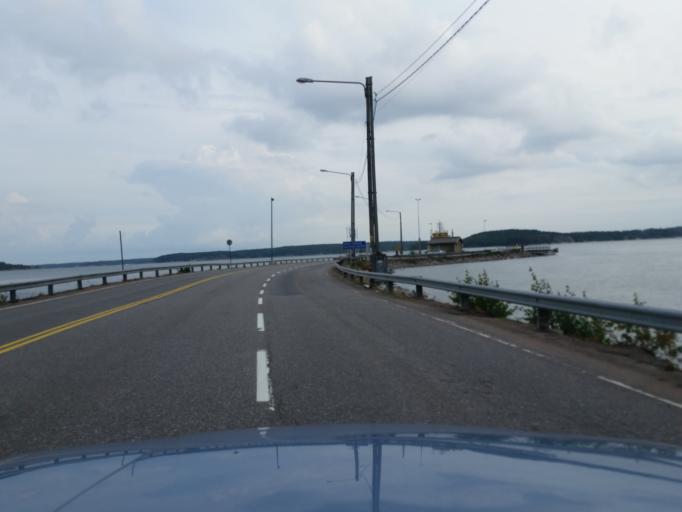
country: FI
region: Varsinais-Suomi
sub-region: Aboland-Turunmaa
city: Nagu
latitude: 60.2210
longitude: 22.0965
